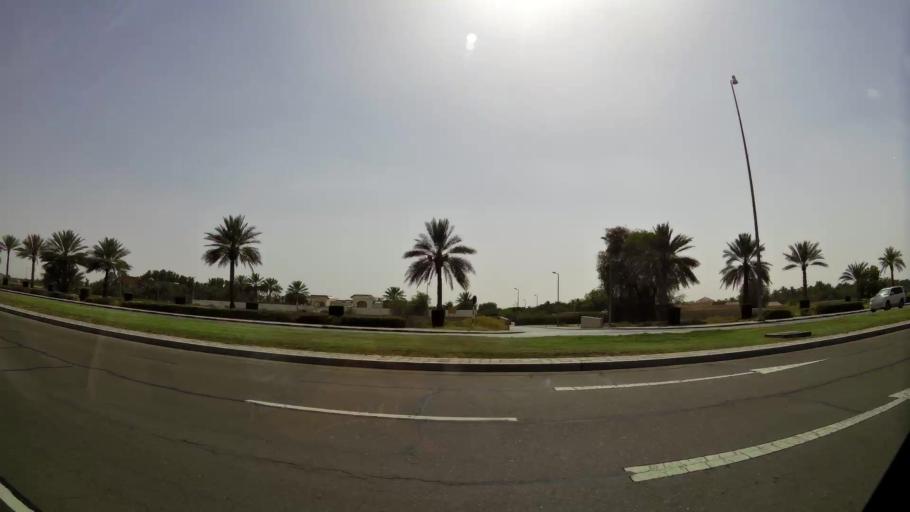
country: AE
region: Abu Dhabi
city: Al Ain
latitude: 24.2270
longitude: 55.6811
